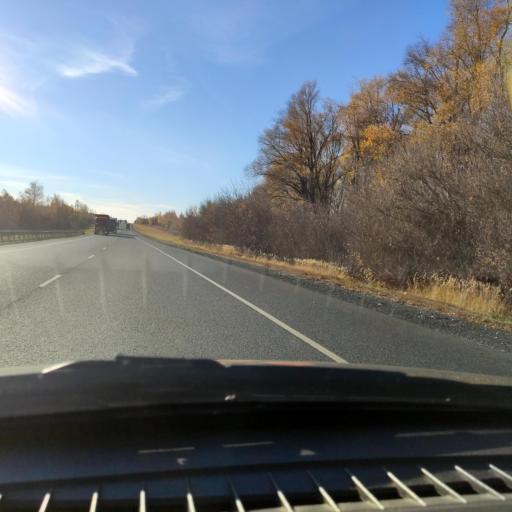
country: RU
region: Samara
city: Mezhdurechensk
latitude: 53.2436
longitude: 48.9826
